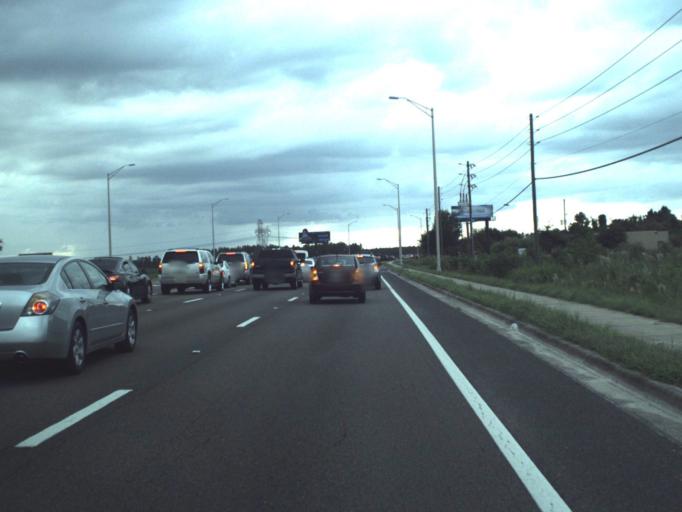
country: US
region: Florida
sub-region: Hillsborough County
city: Keystone
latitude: 28.1943
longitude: -82.6382
